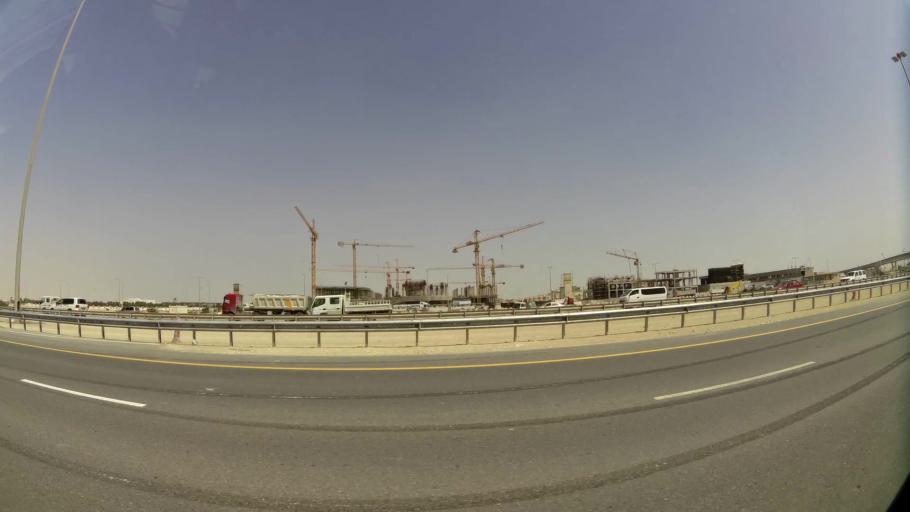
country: QA
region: Baladiyat Umm Salal
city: Umm Salal Muhammad
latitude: 25.4055
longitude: 51.4271
